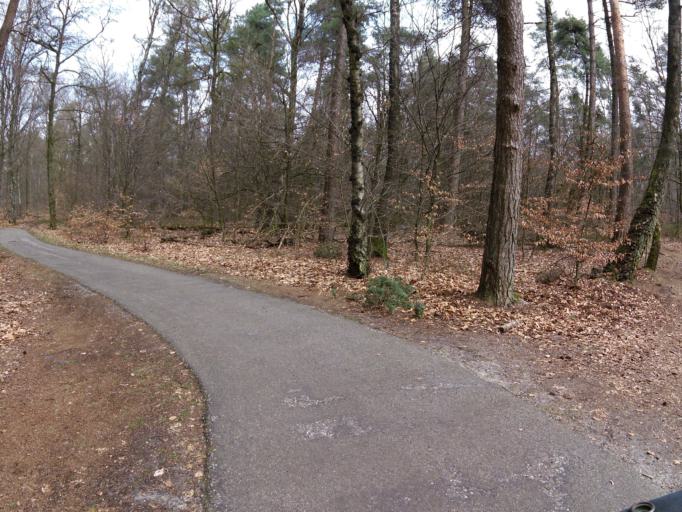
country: NL
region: Gelderland
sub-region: Gemeente Rozendaal
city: Rozendaal
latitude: 52.0181
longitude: 5.9761
